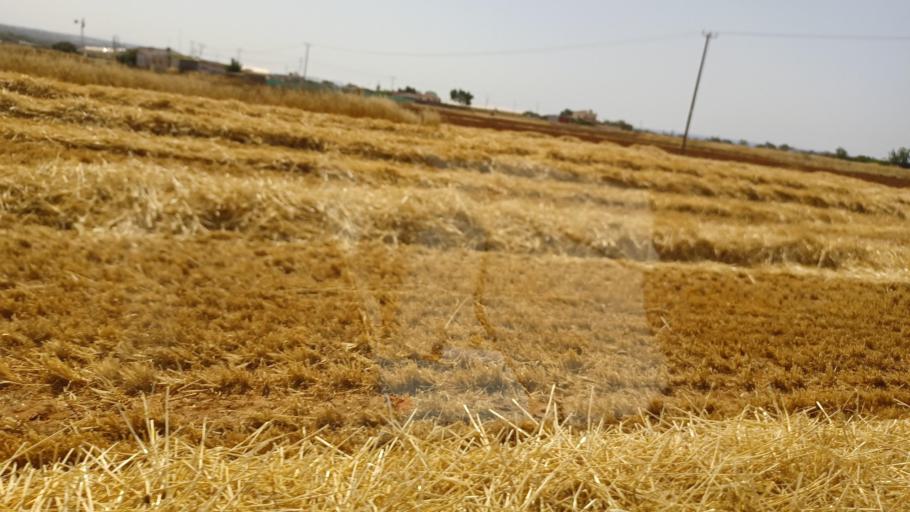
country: CY
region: Ammochostos
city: Frenaros
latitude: 34.9994
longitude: 33.9436
